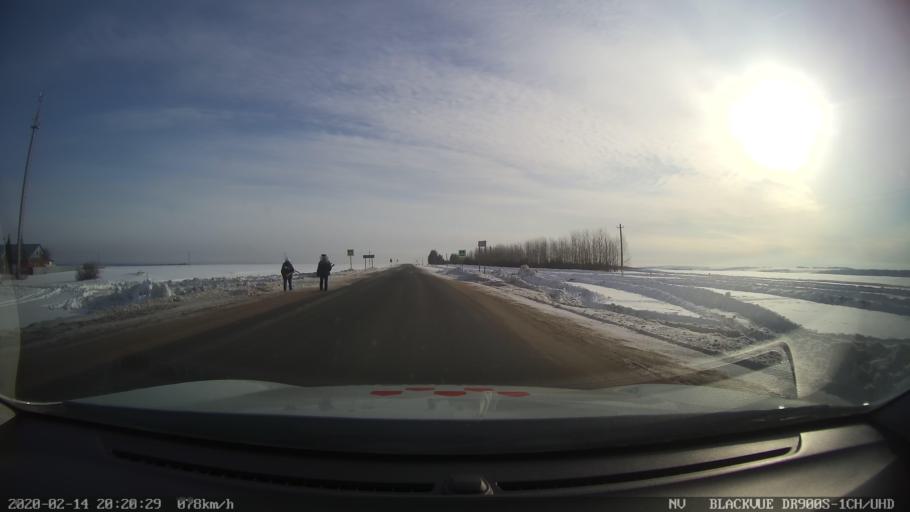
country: RU
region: Tatarstan
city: Verkhniy Uslon
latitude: 55.5570
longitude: 48.9070
